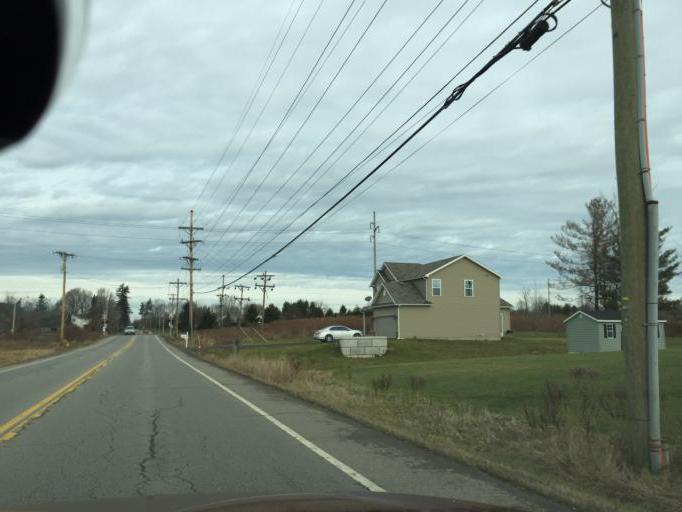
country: US
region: New York
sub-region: Monroe County
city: Scottsville
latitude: 43.0990
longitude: -77.7326
